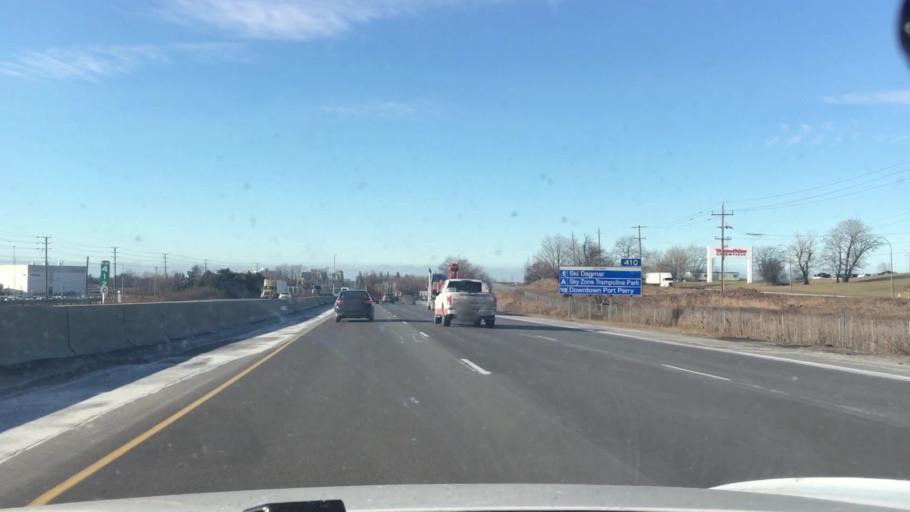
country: CA
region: Ontario
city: Oshawa
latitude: 43.8669
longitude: -78.9162
